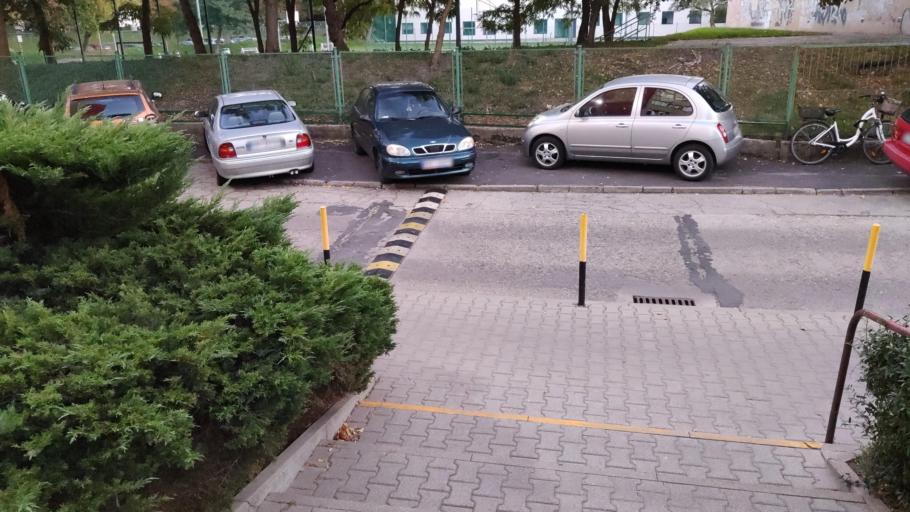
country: PL
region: Lower Silesian Voivodeship
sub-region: Powiat wroclawski
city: Wroclaw
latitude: 51.0886
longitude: 17.0216
